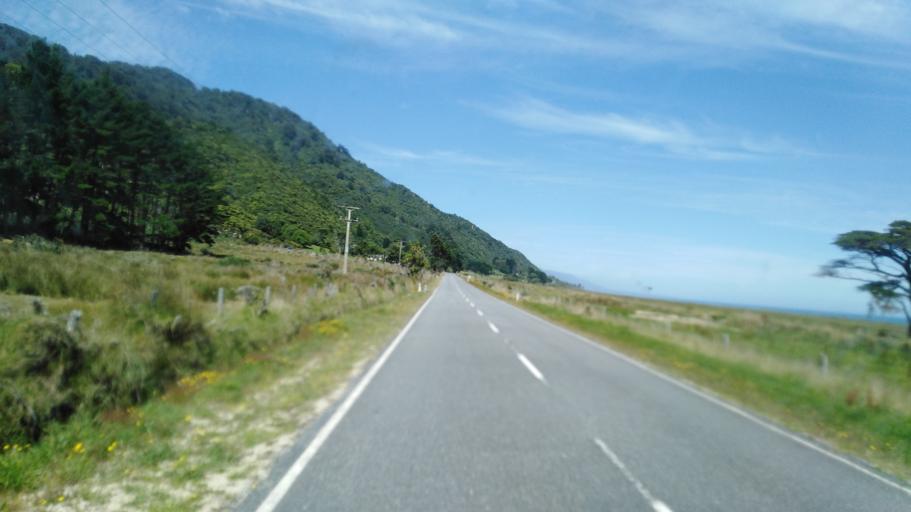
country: NZ
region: West Coast
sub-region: Buller District
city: Westport
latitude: -41.5586
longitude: 171.9174
